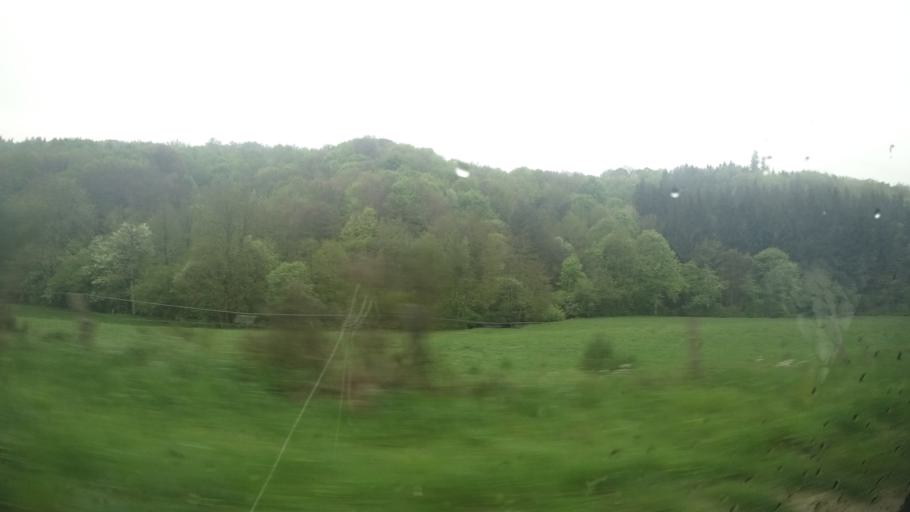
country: FR
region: Midi-Pyrenees
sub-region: Departement de l'Aveyron
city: Salles-Curan
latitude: 44.2660
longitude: 2.8842
